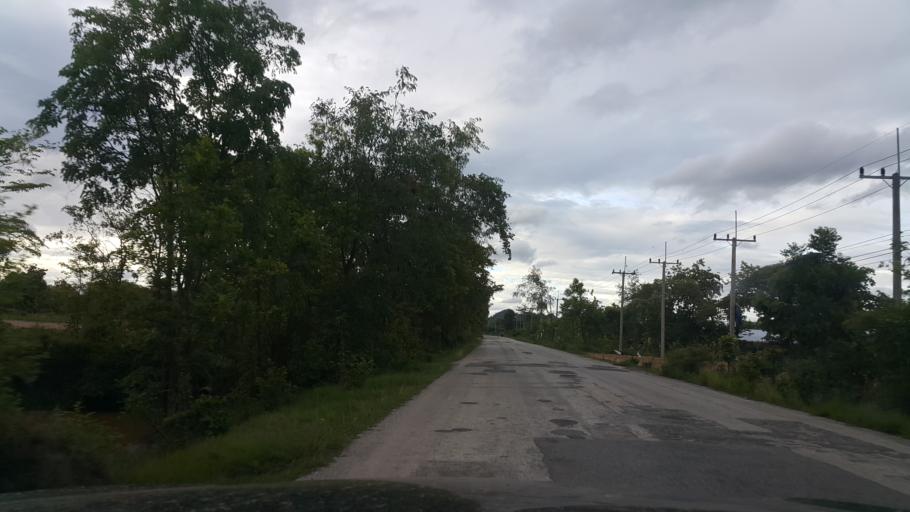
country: TH
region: Sukhothai
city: Thung Saliam
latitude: 17.1739
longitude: 99.5249
